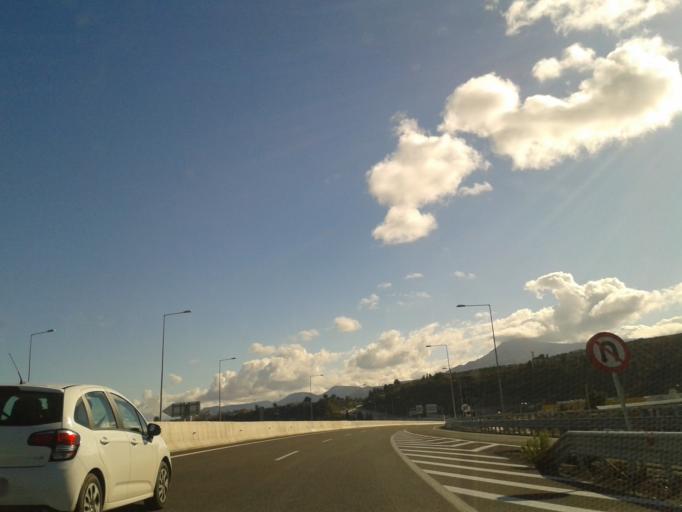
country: GR
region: West Greece
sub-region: Nomos Achaias
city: Aigio
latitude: 38.2633
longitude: 22.0585
